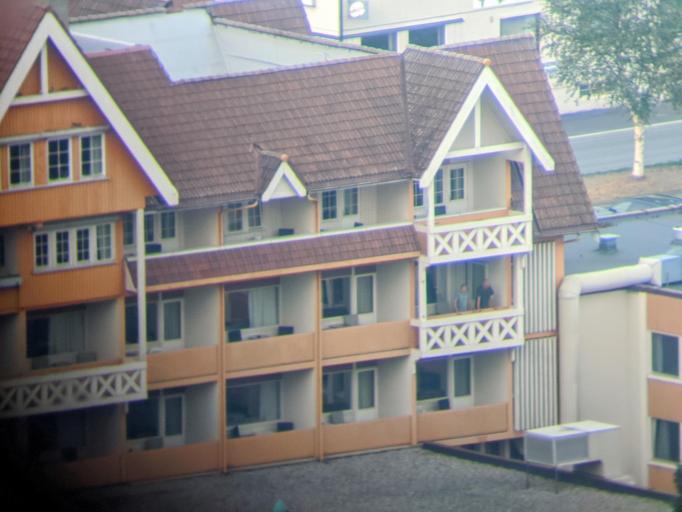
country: NO
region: Oppland
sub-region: Nord-Aurdal
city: Fagernes
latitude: 60.9808
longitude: 9.2200
